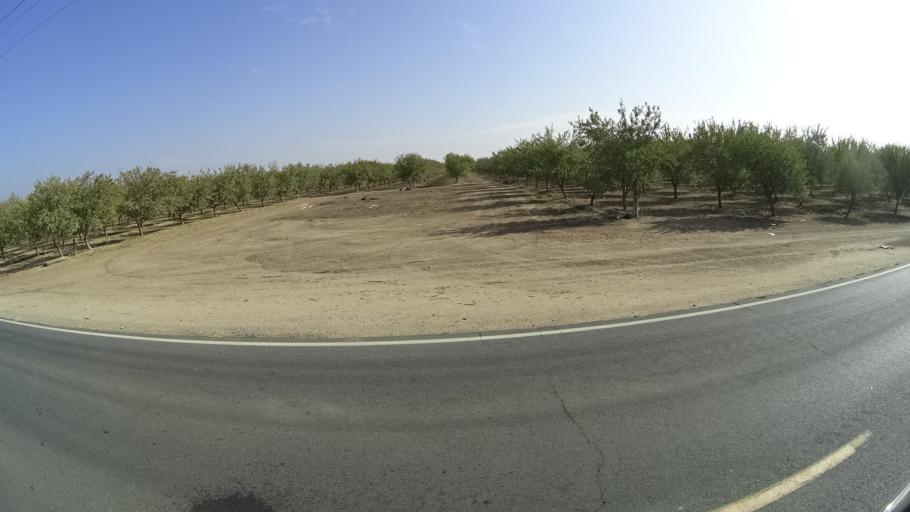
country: US
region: California
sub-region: Kern County
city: Delano
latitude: 35.7362
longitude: -119.2231
